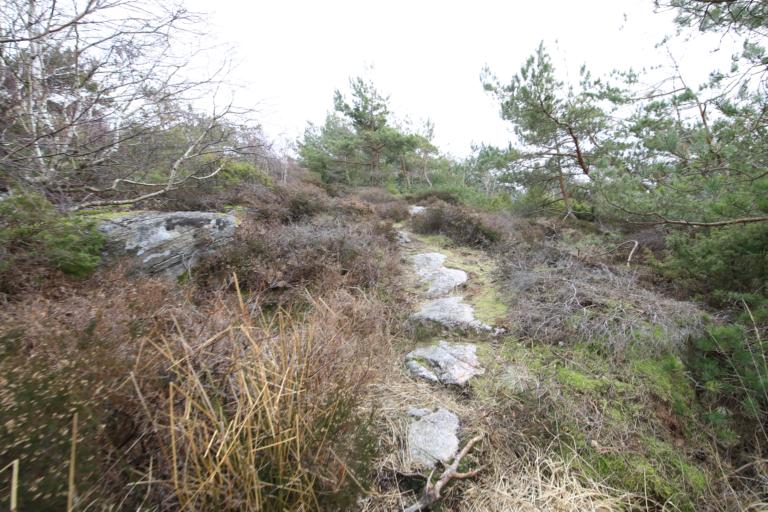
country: SE
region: Halland
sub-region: Kungsbacka Kommun
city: Frillesas
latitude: 57.2365
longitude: 12.0989
